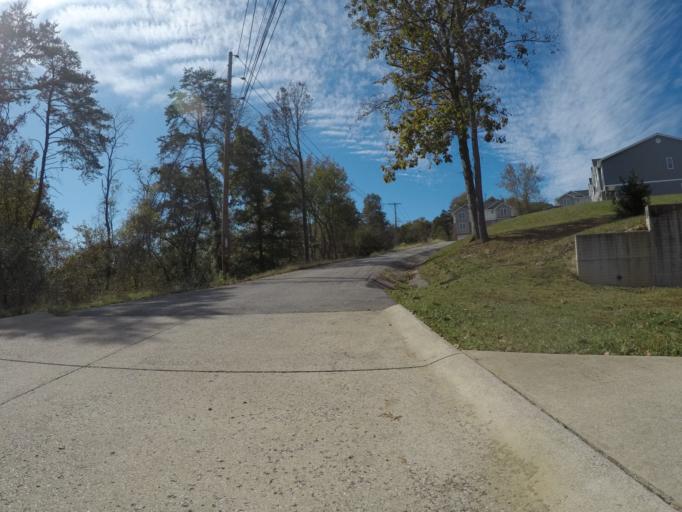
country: US
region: West Virginia
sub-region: Cabell County
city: Huntington
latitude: 38.3939
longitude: -82.3877
